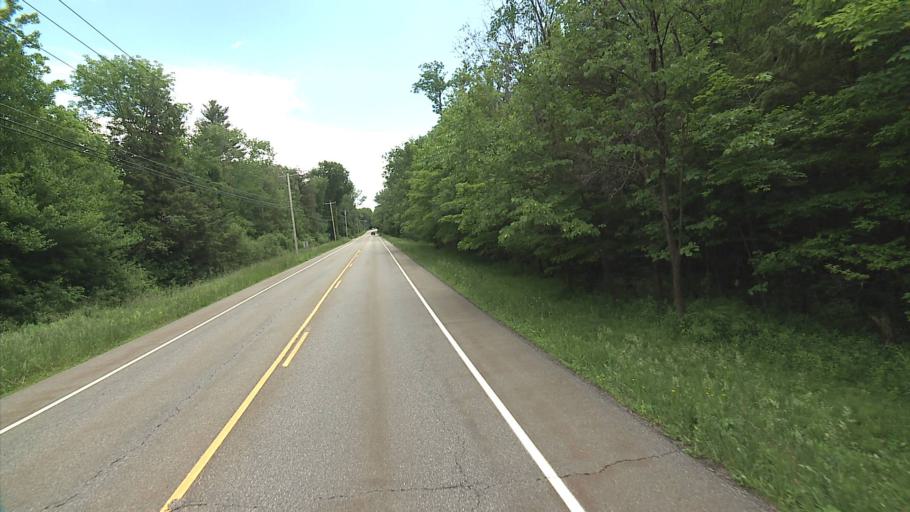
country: US
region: Connecticut
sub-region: Litchfield County
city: West Torrington
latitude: 41.8482
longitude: -73.2395
